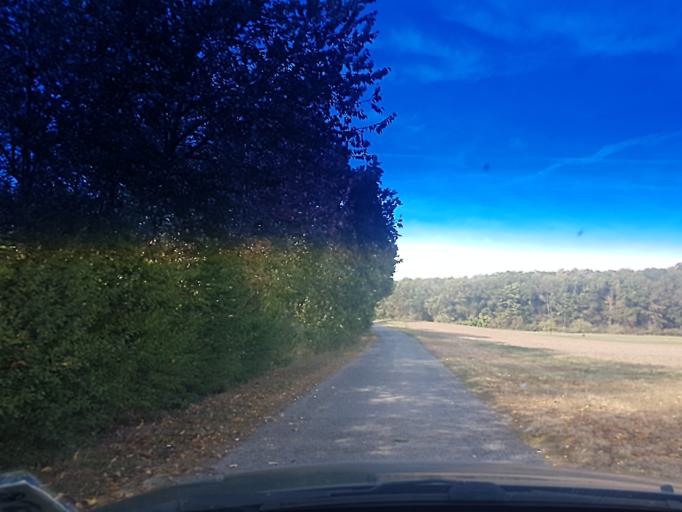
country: DE
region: Bavaria
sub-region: Regierungsbezirk Mittelfranken
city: Burghaslach
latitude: 49.7694
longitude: 10.5433
